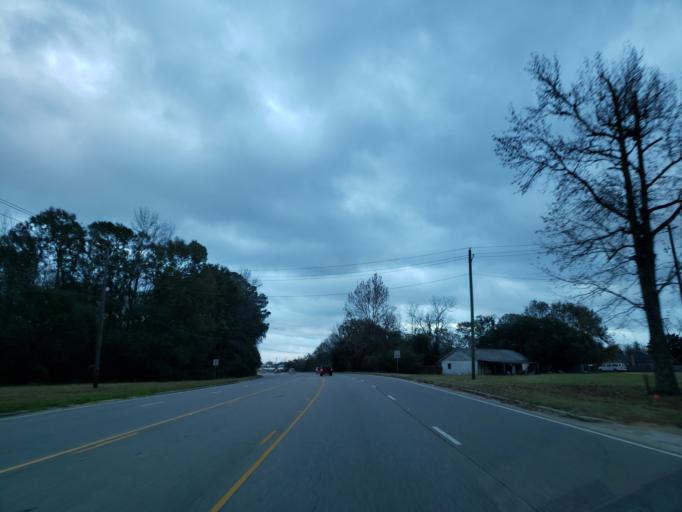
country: US
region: Alabama
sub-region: Mobile County
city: Prichard
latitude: 30.7804
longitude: -88.2691
